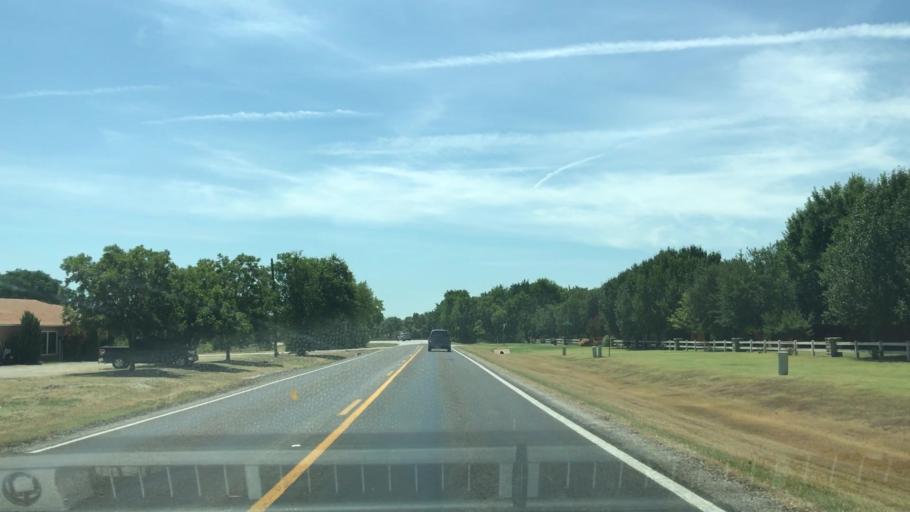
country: US
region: Texas
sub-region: Collin County
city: Fairview
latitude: 33.1221
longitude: -96.6096
